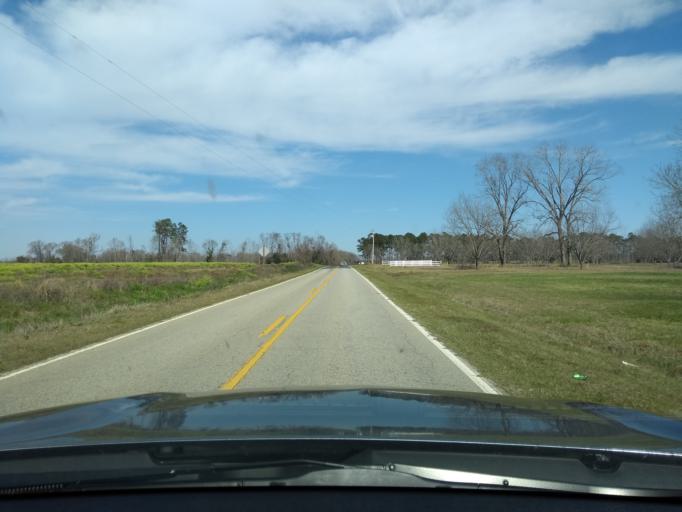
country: US
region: Georgia
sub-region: Bulloch County
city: Brooklet
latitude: 32.4599
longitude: -81.6565
